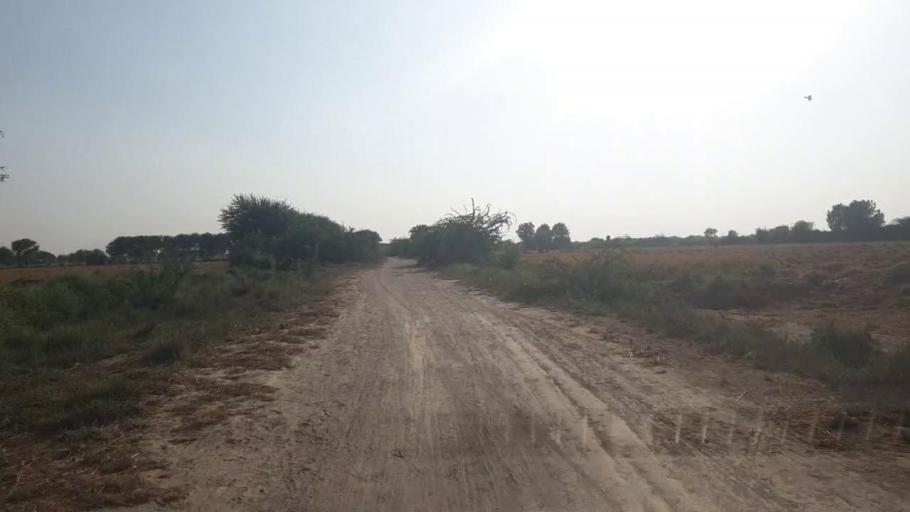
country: PK
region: Sindh
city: Badin
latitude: 24.6391
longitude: 68.8000
